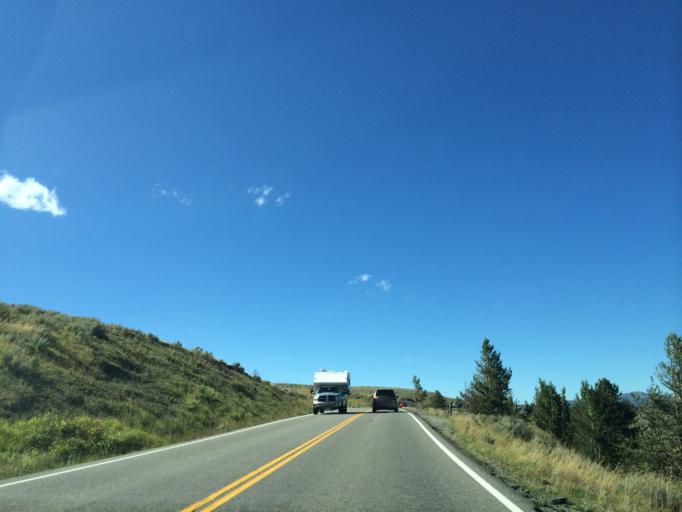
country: US
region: Montana
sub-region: Gallatin County
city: West Yellowstone
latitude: 44.6310
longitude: -110.4444
